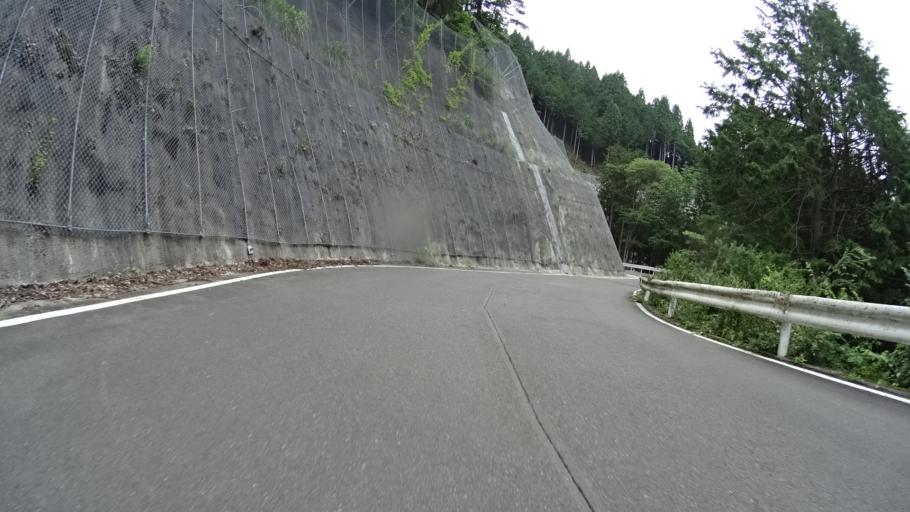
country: JP
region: Kanagawa
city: Hadano
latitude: 35.4819
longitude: 139.2112
